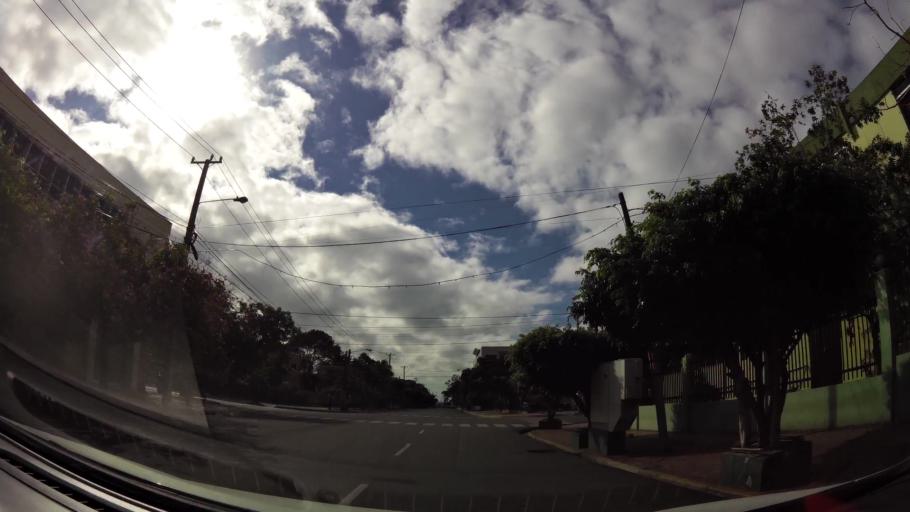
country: DO
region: Nacional
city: La Julia
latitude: 18.4513
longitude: -69.9260
